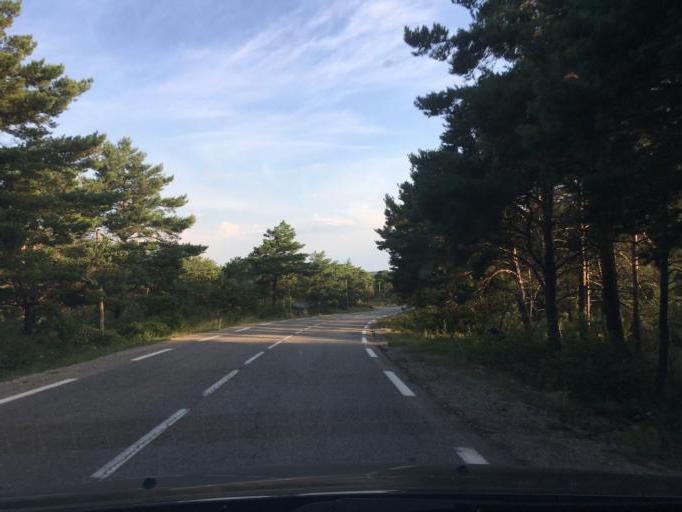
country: FR
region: Provence-Alpes-Cote d'Azur
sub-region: Departement du Var
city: Aups
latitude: 43.6691
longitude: 6.2252
